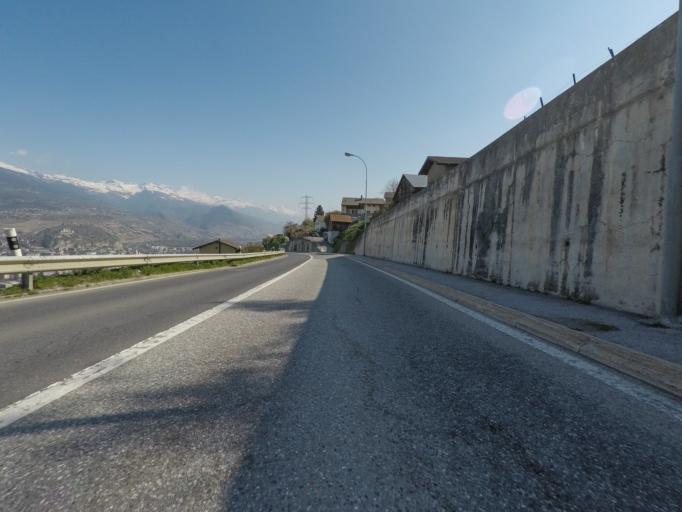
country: CH
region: Valais
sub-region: Sion District
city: Sitten
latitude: 46.2130
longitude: 7.3503
